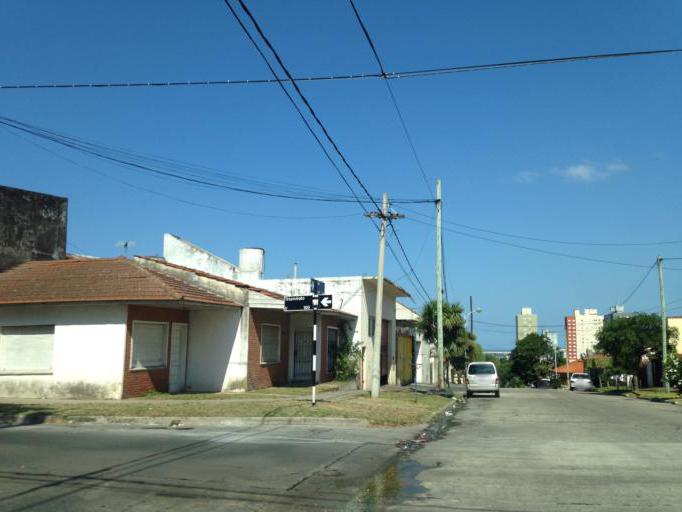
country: AR
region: Buenos Aires
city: Mar del Plata
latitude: -38.0368
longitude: -57.5493
